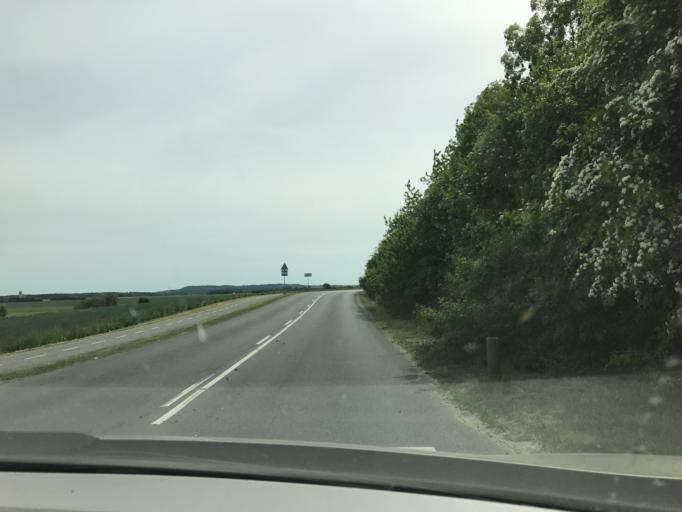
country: DK
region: Central Jutland
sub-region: Norddjurs Kommune
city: Allingabro
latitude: 56.4960
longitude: 10.3305
